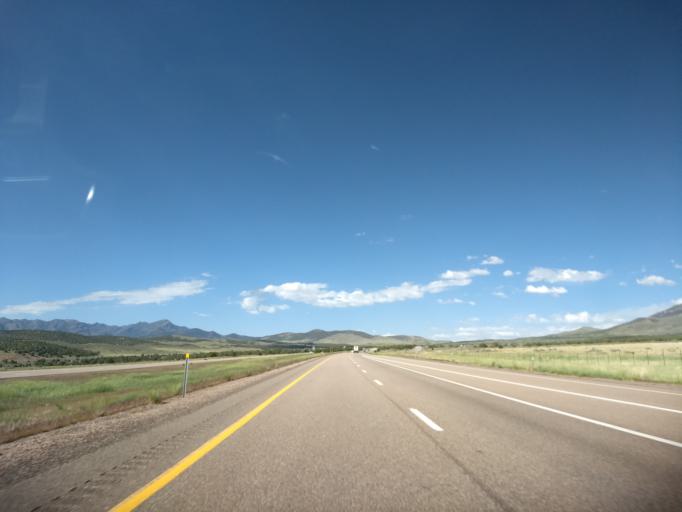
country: US
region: Utah
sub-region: Millard County
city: Fillmore
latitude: 39.1487
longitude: -112.2331
